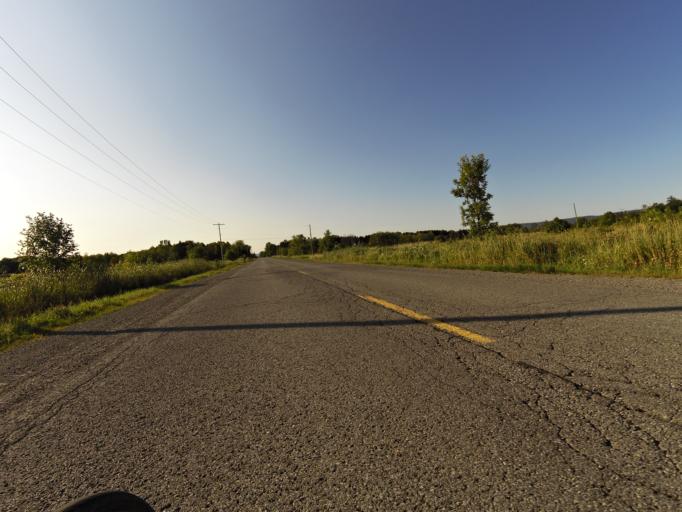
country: CA
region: Ontario
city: Bells Corners
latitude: 45.4567
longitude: -75.9944
